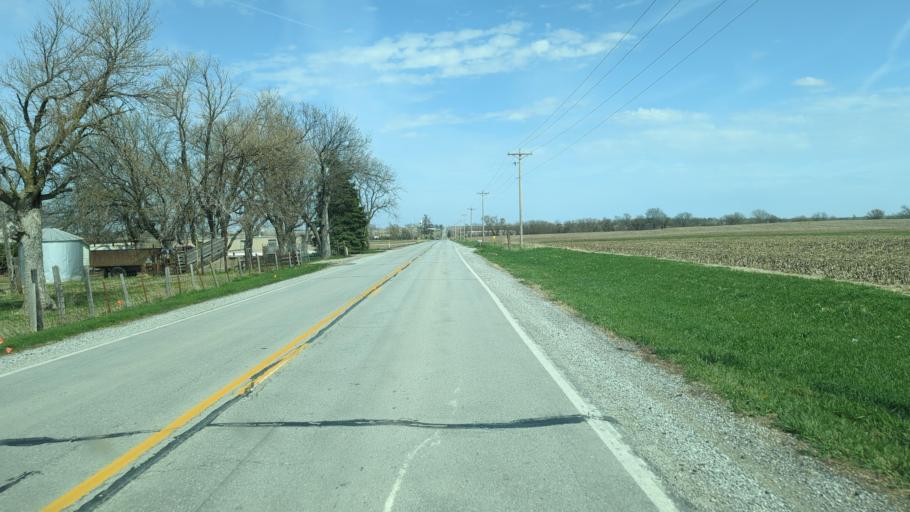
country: US
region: Nebraska
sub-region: Sarpy County
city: Springfield
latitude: 41.0889
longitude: -96.1542
